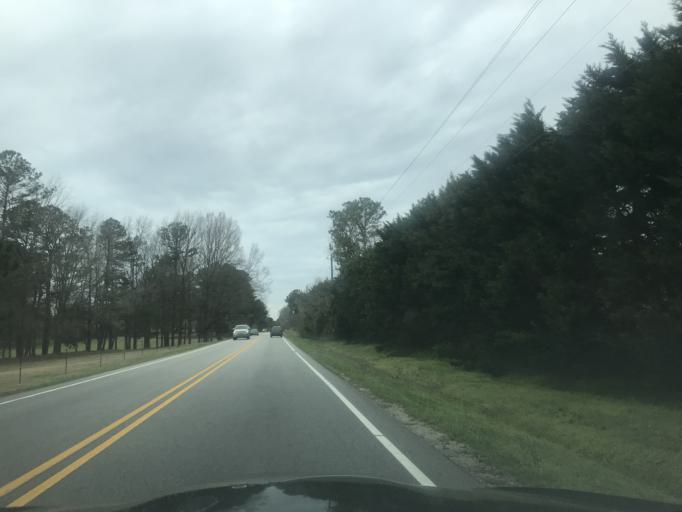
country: US
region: North Carolina
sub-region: Franklin County
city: Franklinton
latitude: 36.1085
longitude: -78.4740
